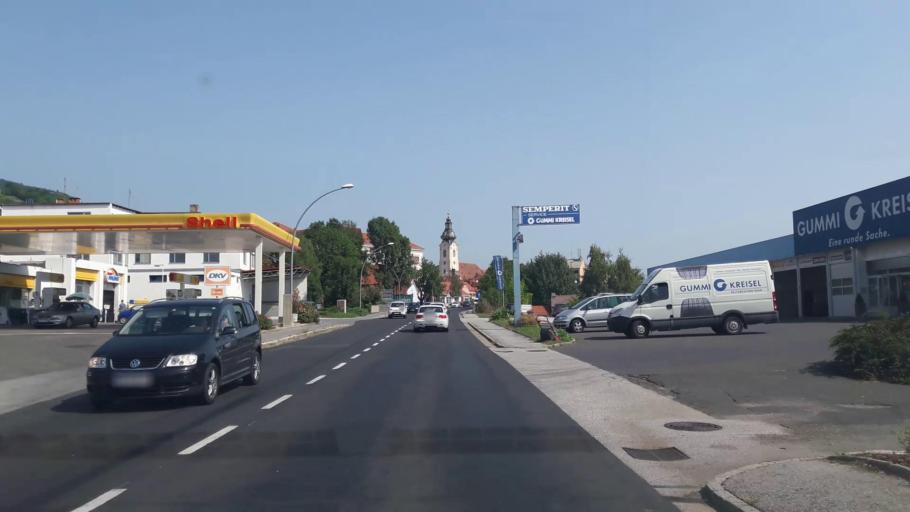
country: AT
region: Styria
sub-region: Politischer Bezirk Hartberg-Fuerstenfeld
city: Hartberg
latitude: 47.2769
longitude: 15.9673
